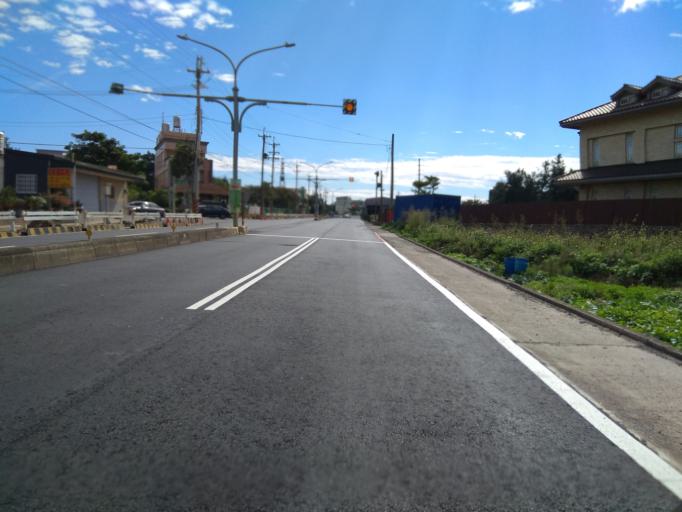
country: TW
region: Taiwan
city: Taoyuan City
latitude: 25.0573
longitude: 121.1370
